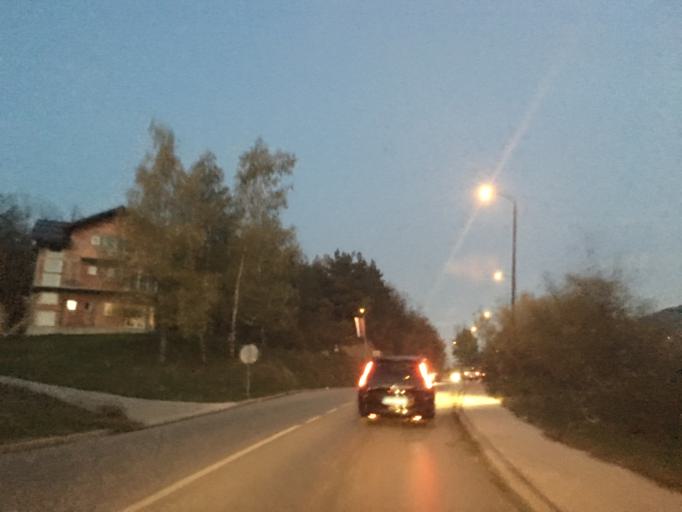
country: BA
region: Federation of Bosnia and Herzegovina
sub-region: Kanton Sarajevo
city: Sarajevo
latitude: 43.8414
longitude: 18.3959
